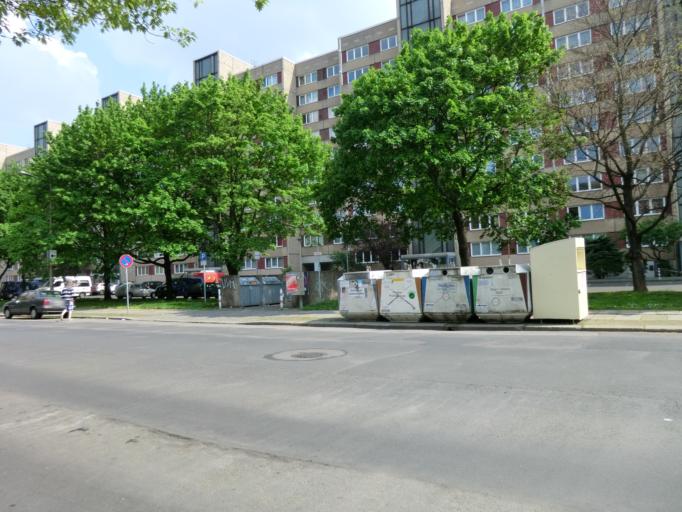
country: DE
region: Saxony
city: Dresden
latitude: 51.0557
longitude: 13.7630
